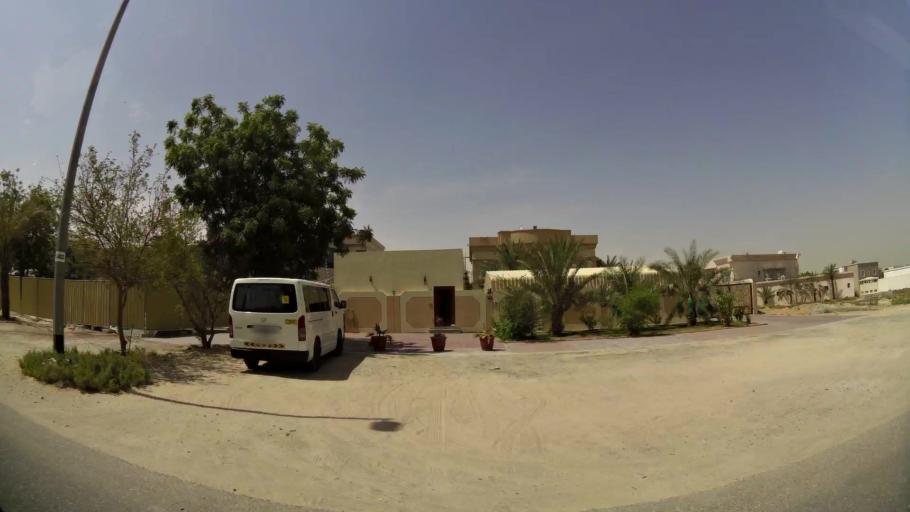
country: AE
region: Ash Shariqah
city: Sharjah
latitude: 25.1791
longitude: 55.4231
